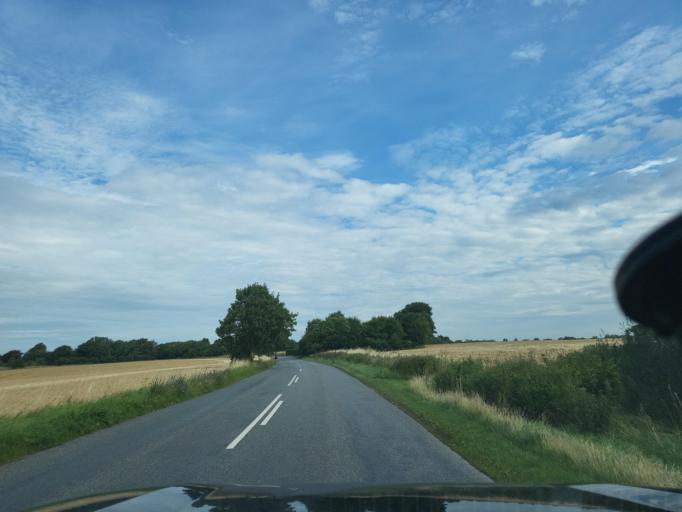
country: DK
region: Zealand
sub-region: Kalundborg Kommune
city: Svebolle
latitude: 55.7453
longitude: 11.3406
